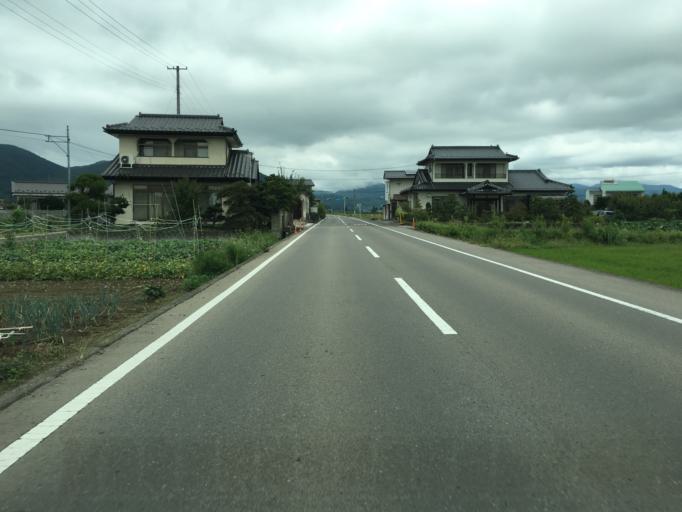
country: JP
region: Fukushima
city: Fukushima-shi
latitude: 37.7862
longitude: 140.4097
